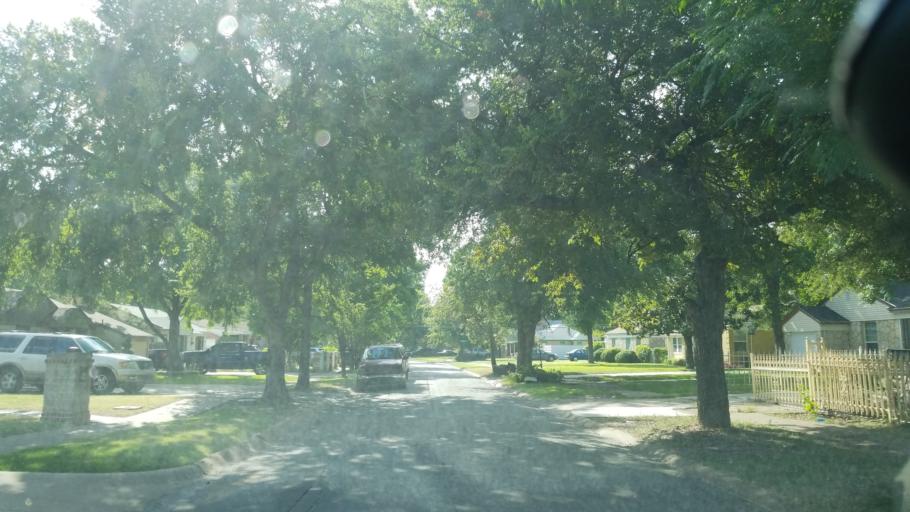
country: US
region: Texas
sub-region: Dallas County
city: Dallas
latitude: 32.7699
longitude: -96.7158
